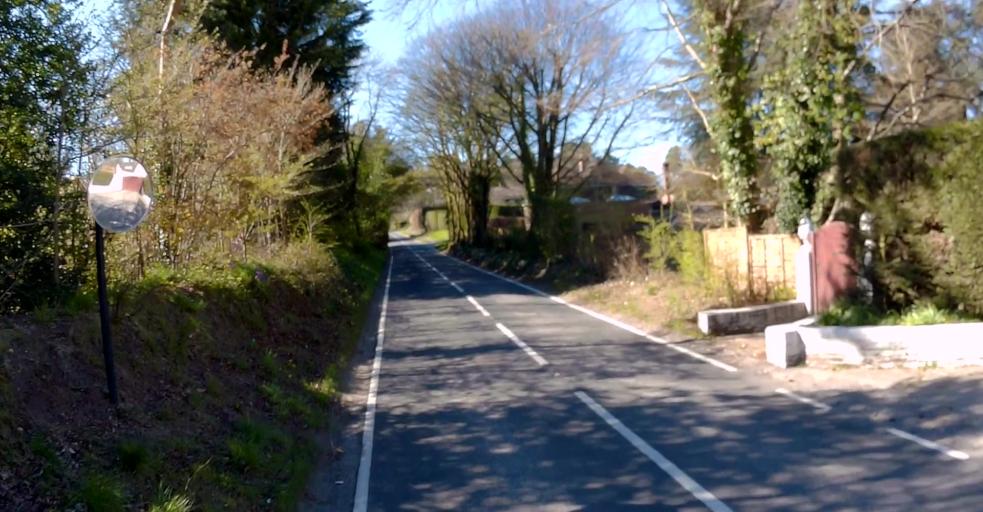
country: GB
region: England
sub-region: Surrey
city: Farnham
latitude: 51.2051
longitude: -0.7803
